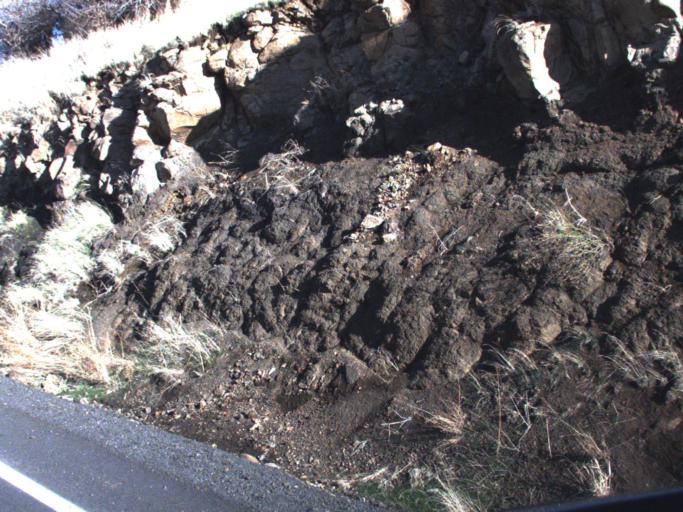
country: US
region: Washington
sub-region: Whitman County
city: Colfax
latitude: 46.7197
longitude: -117.4842
